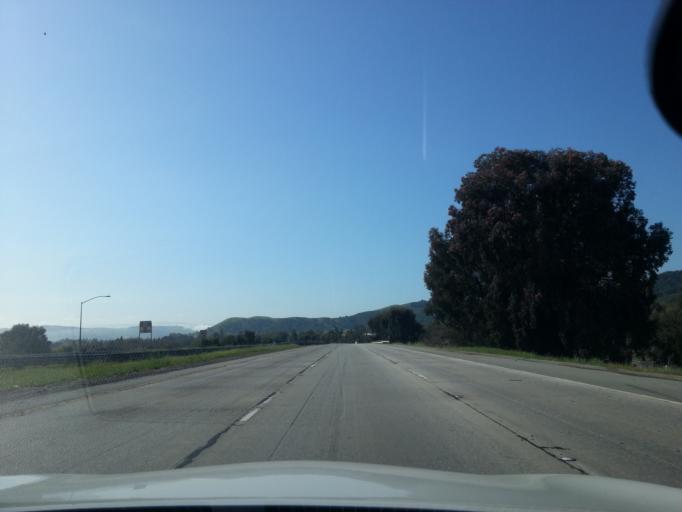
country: US
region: California
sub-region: Santa Clara County
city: Gilroy
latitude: 36.9887
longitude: -121.5583
